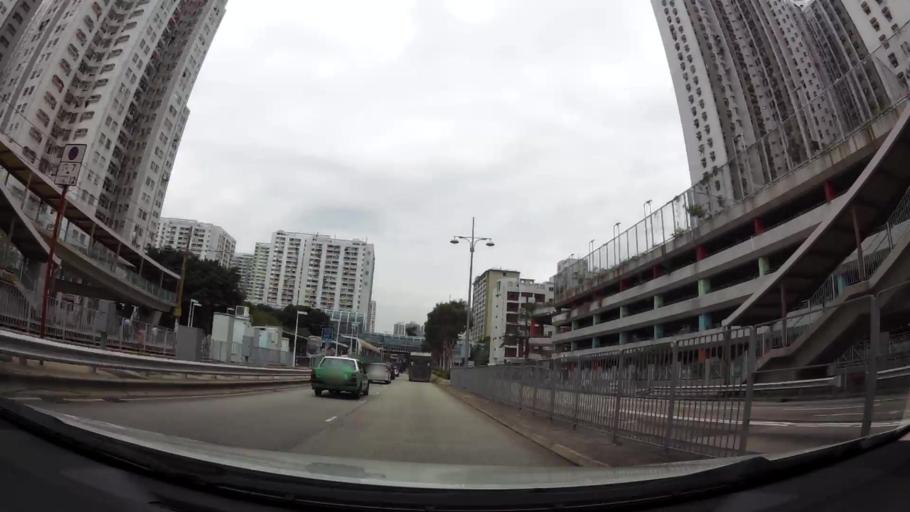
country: HK
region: Tuen Mun
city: Tuen Mun
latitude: 22.3840
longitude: 113.9752
